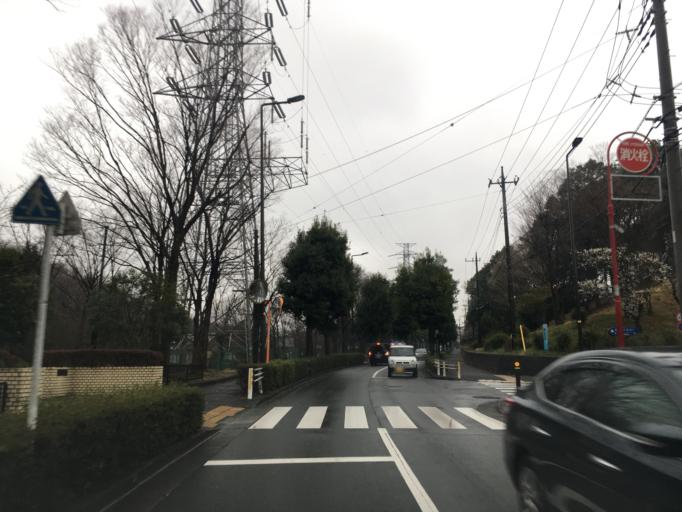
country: JP
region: Tokyo
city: Kokubunji
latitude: 35.6349
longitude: 139.4591
